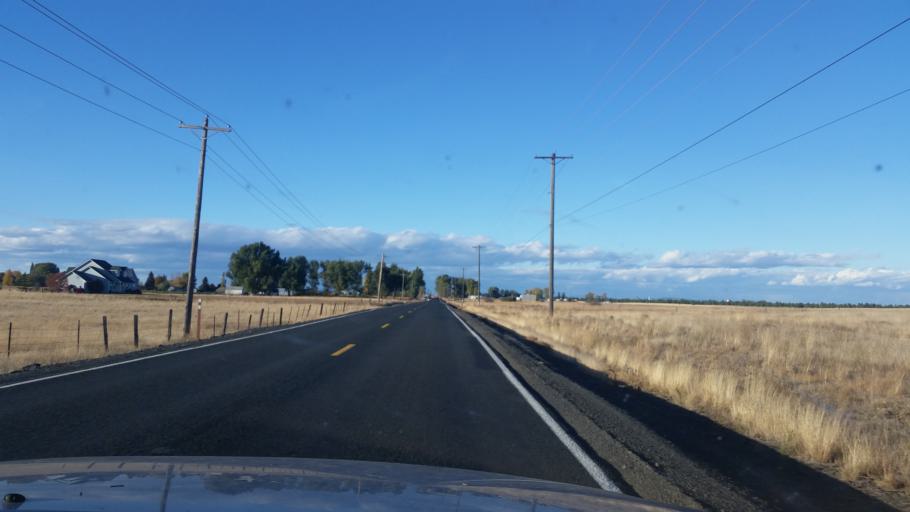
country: US
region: Washington
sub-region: Spokane County
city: Airway Heights
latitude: 47.6035
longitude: -117.6075
